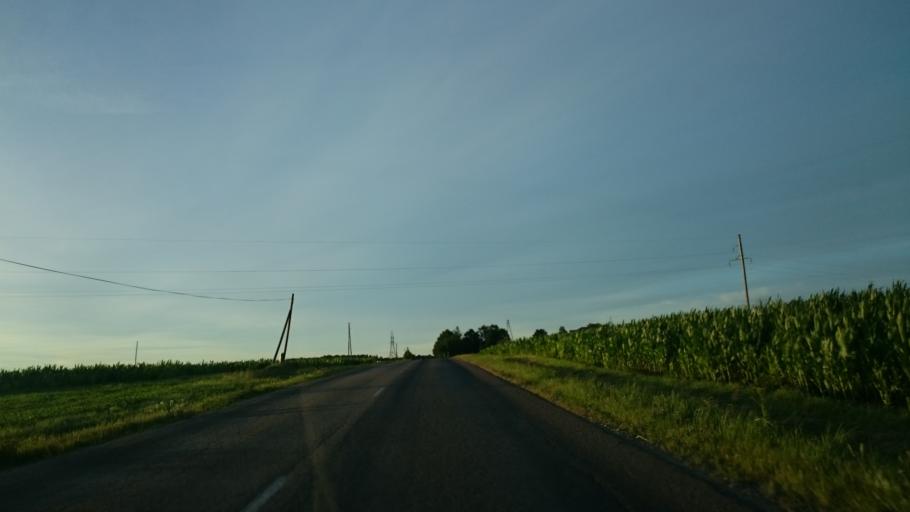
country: LV
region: Saldus Rajons
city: Saldus
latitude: 56.6844
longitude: 22.5032
